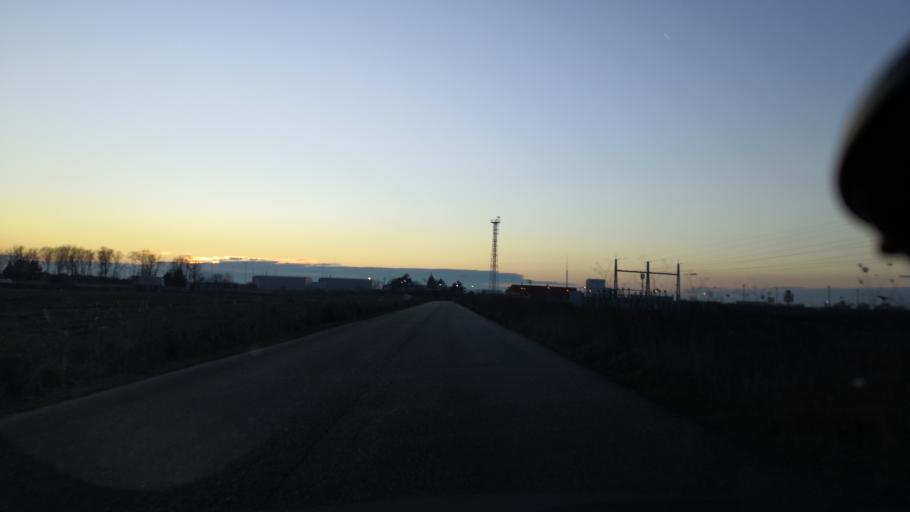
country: RS
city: Simanovci
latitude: 44.8809
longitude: 20.1239
